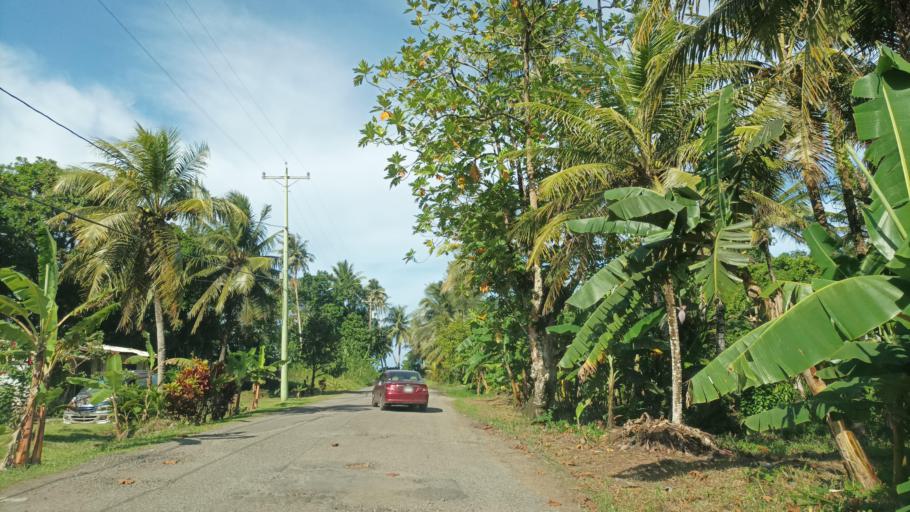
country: FM
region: Kosrae
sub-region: Lelu Municipality
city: Lelu
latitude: 5.3209
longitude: 163.0281
